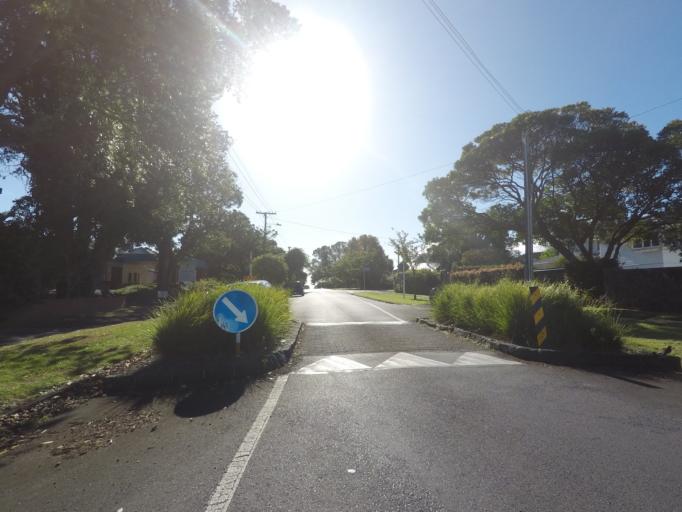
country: NZ
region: Auckland
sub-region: Auckland
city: Rosebank
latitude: -36.8892
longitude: 174.7134
